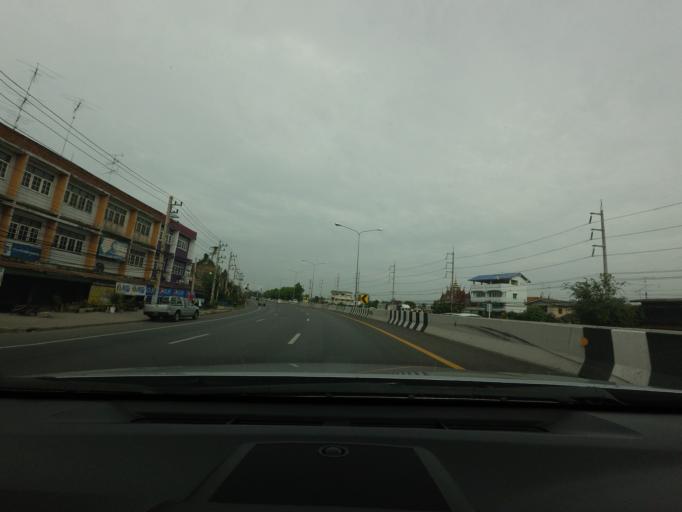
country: TH
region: Phetchaburi
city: Phetchaburi
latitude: 13.1256
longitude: 99.8763
